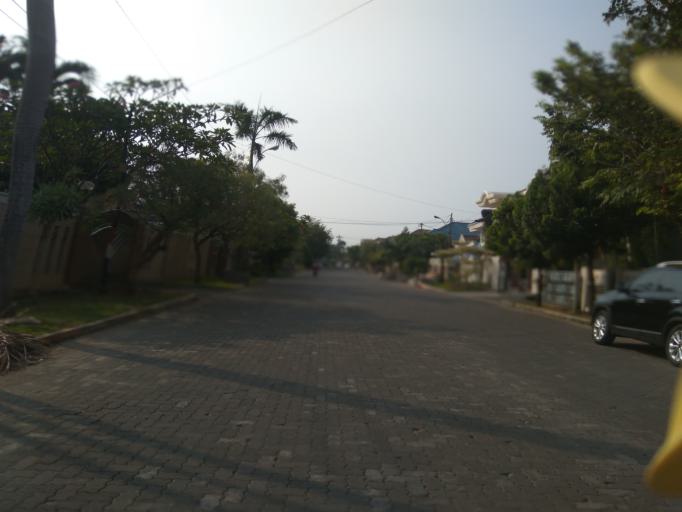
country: ID
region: Central Java
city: Semarang
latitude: -6.9669
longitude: 110.3862
